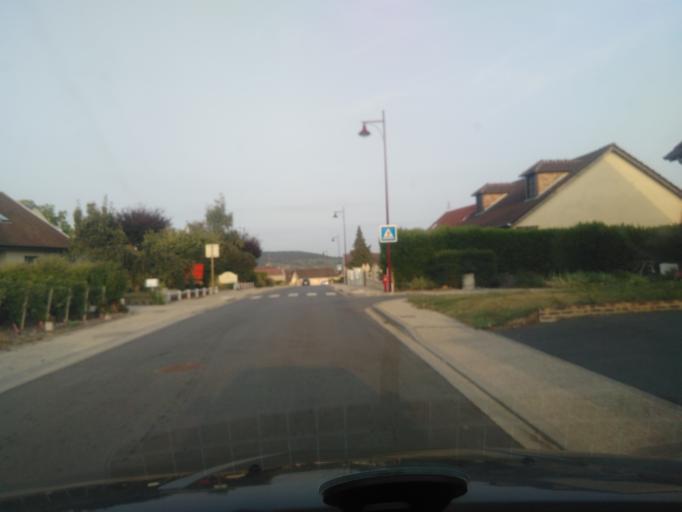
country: FR
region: Champagne-Ardenne
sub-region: Departement de la Marne
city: Damery
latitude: 49.0811
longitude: 3.8514
